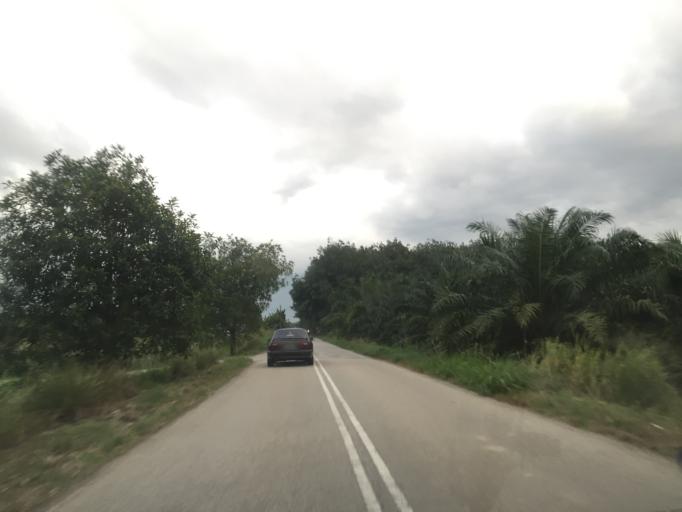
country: MY
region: Penang
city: Tasek Glugor
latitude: 5.5362
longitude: 100.5131
